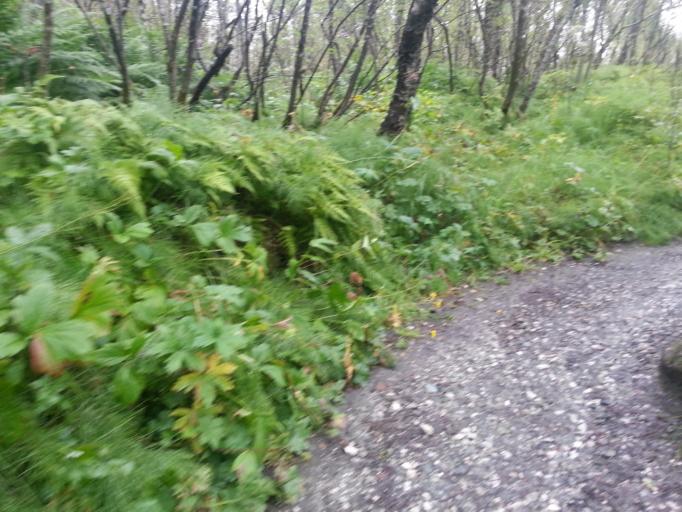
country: NO
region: Troms
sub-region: Tromso
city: Tromso
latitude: 69.6773
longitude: 18.9734
